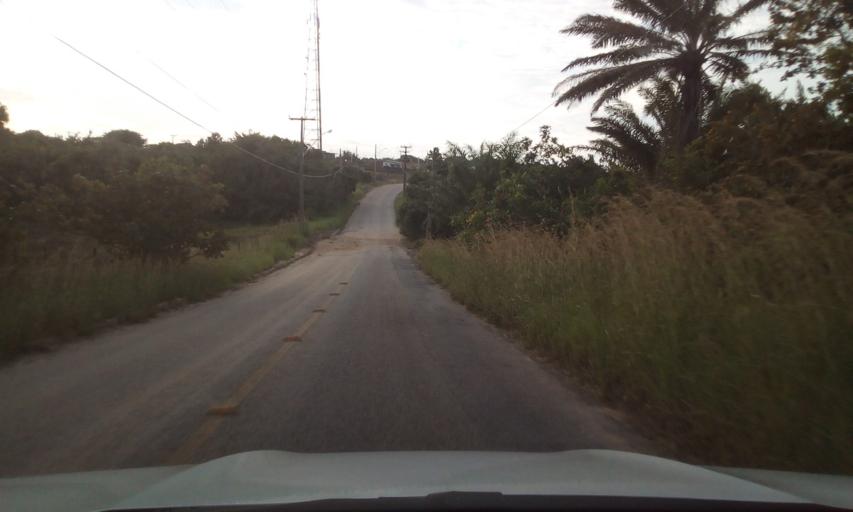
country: BR
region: Paraiba
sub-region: Conde
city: Conde
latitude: -7.2213
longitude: -34.8106
